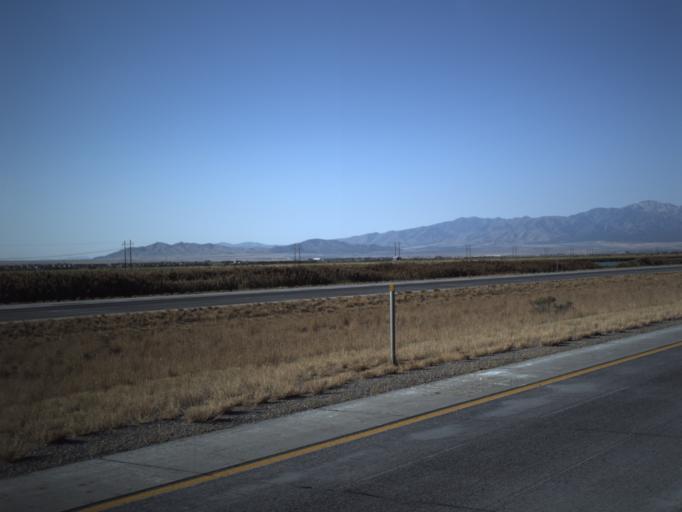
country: US
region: Utah
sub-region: Tooele County
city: Stansbury park
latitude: 40.6672
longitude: -112.3069
